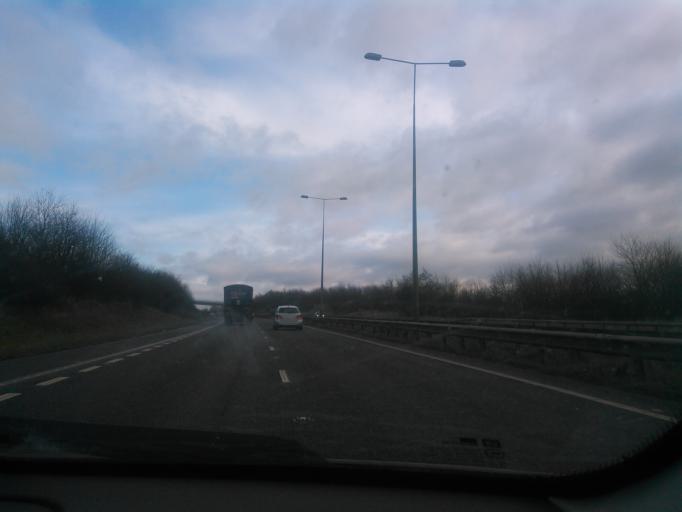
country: GB
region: England
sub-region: Derbyshire
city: Melbourne
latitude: 52.8602
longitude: -1.4315
